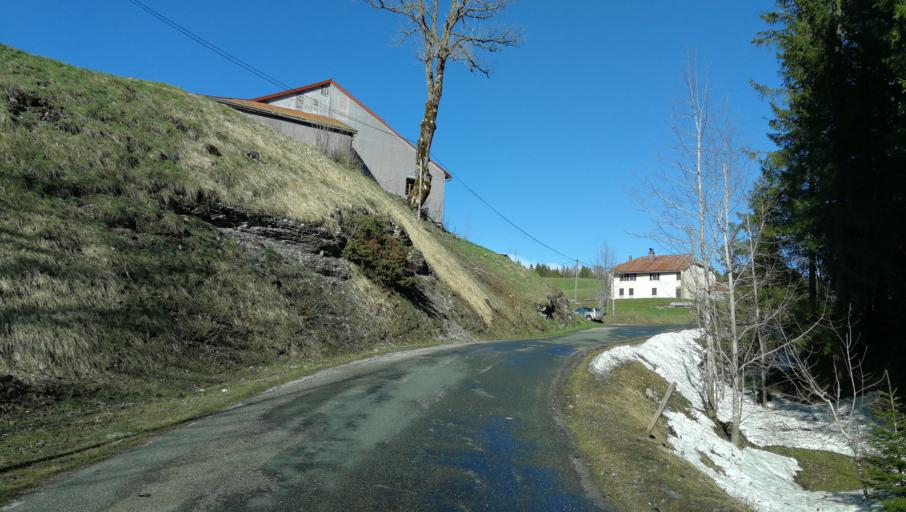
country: FR
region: Franche-Comte
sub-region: Departement du Jura
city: Saint-Claude
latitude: 46.3059
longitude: 5.8910
